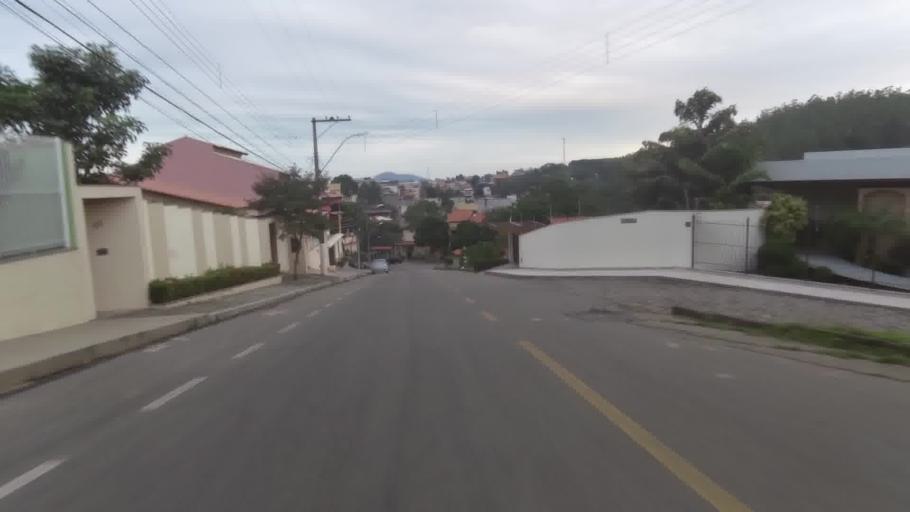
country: BR
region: Espirito Santo
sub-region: Iconha
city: Iconha
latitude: -20.7886
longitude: -40.8135
